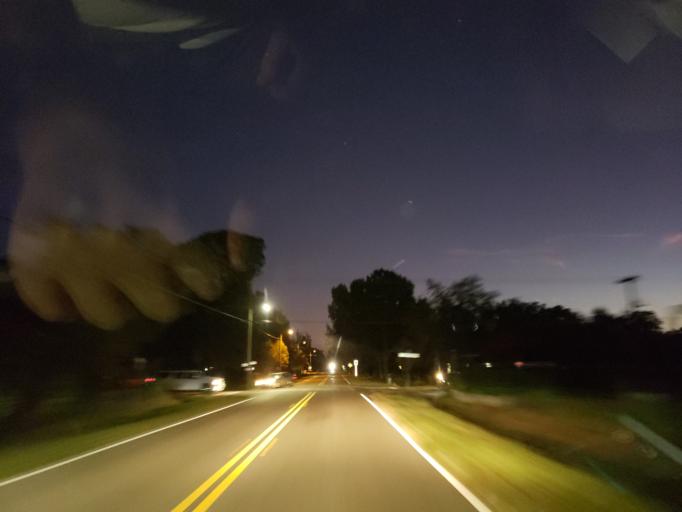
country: US
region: Florida
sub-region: Hillsborough County
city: Dover
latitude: 27.9821
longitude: -82.2198
